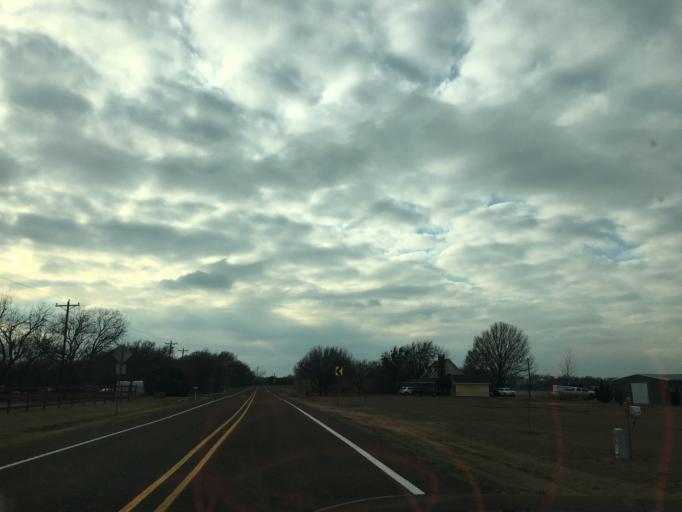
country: US
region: Texas
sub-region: Ellis County
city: Palmer
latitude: 32.4483
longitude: -96.7144
